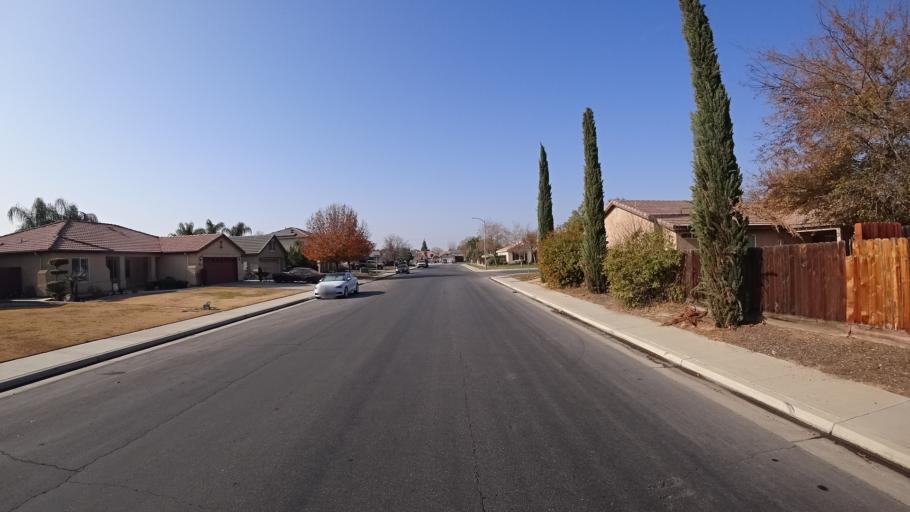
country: US
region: California
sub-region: Kern County
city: Greenacres
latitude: 35.4183
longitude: -119.1255
